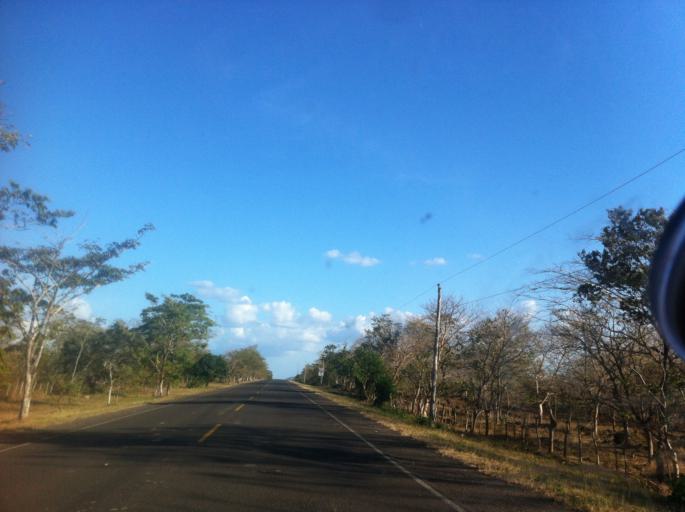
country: NI
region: Rio San Juan
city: Morrito
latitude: 11.7428
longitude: -84.9876
